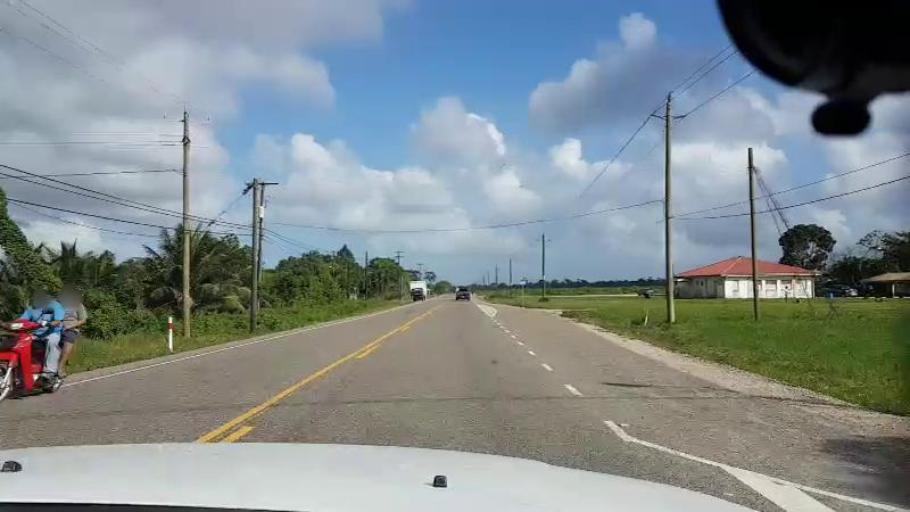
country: BZ
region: Stann Creek
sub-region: Dangriga
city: Dangriga
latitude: 16.9980
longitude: -88.3485
